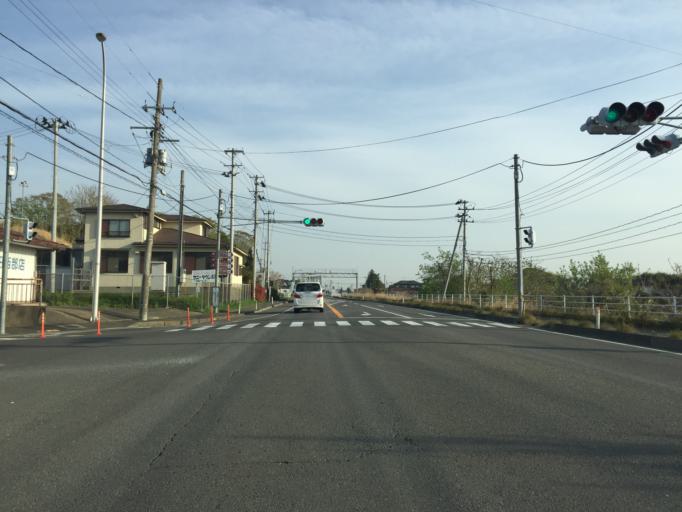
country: JP
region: Miyagi
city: Watari
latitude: 38.0085
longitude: 140.8626
